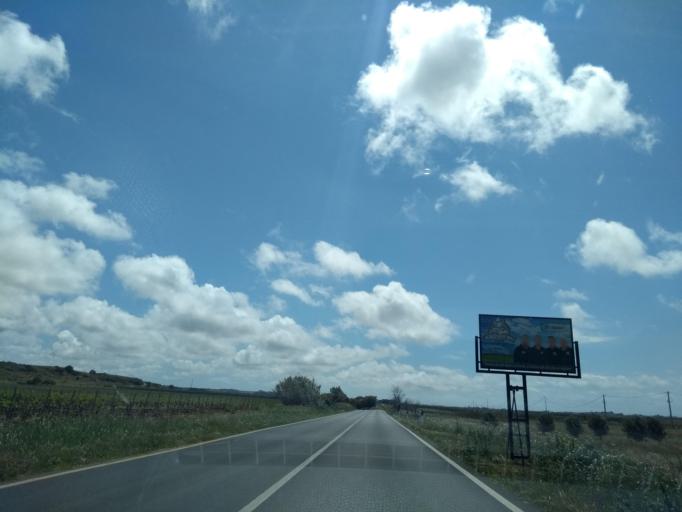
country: IT
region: Sicily
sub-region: Trapani
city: Rilievo
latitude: 37.8913
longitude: 12.5270
